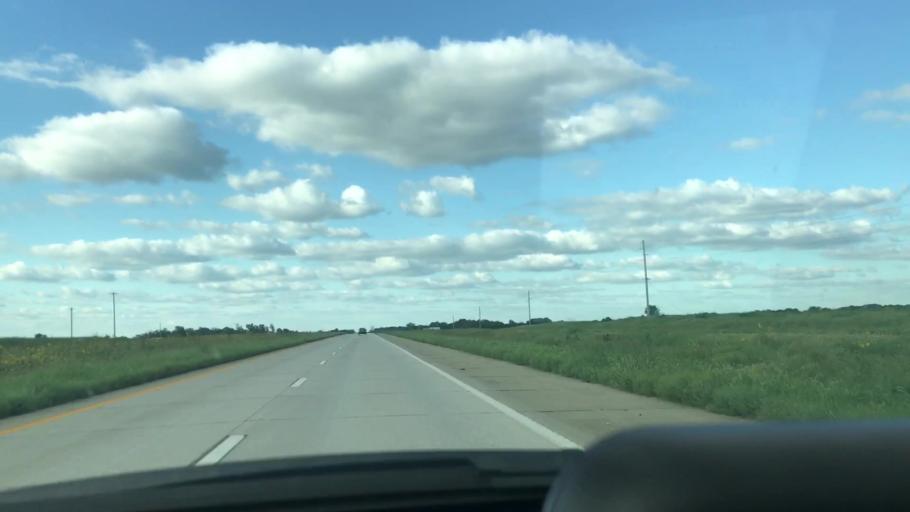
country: US
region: Missouri
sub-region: Benton County
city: Cole Camp
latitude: 38.5146
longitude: -93.2725
